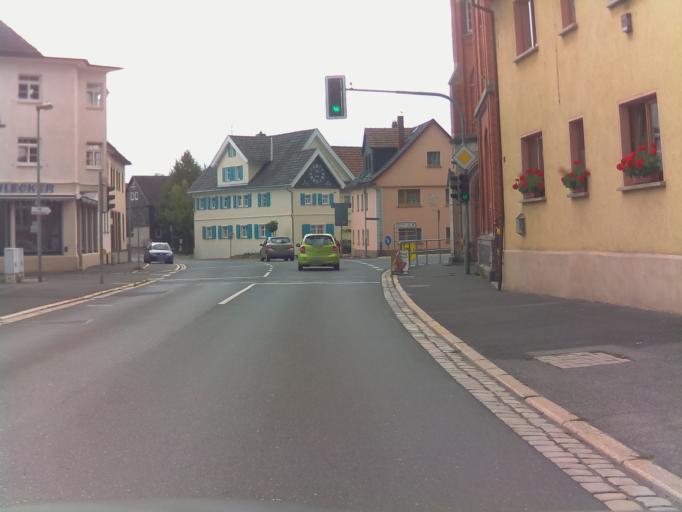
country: DE
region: Thuringia
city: Sonneberg
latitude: 50.3418
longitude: 11.1822
